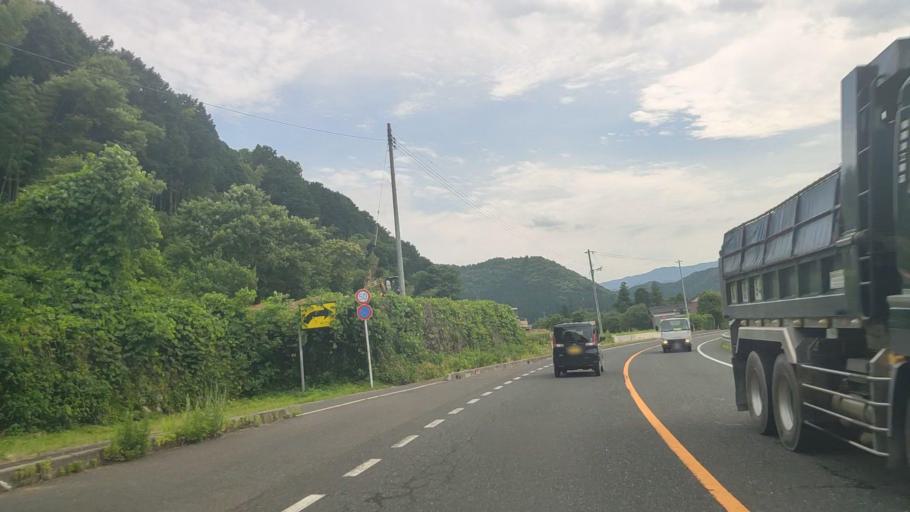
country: JP
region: Tottori
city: Tottori
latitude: 35.3611
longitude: 134.2129
